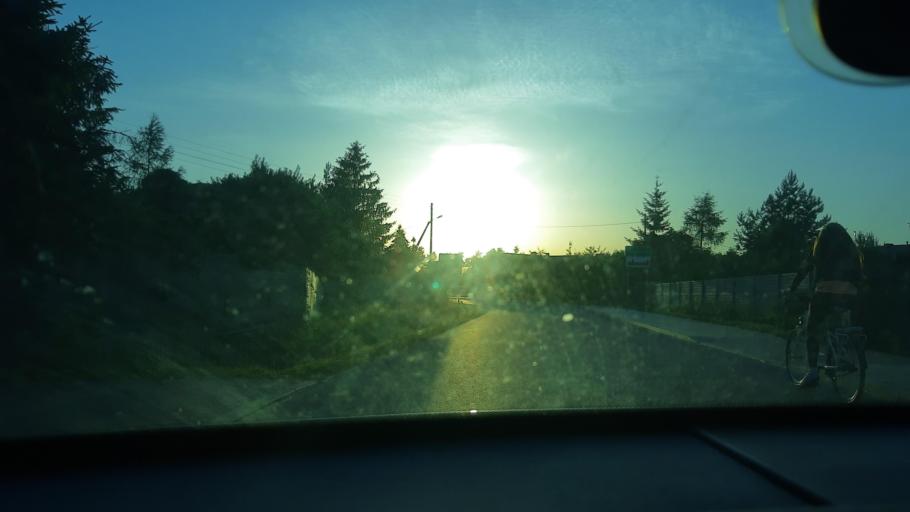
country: PL
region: Lodz Voivodeship
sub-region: Powiat zdunskowolski
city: Zdunska Wola
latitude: 51.6071
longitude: 18.9842
